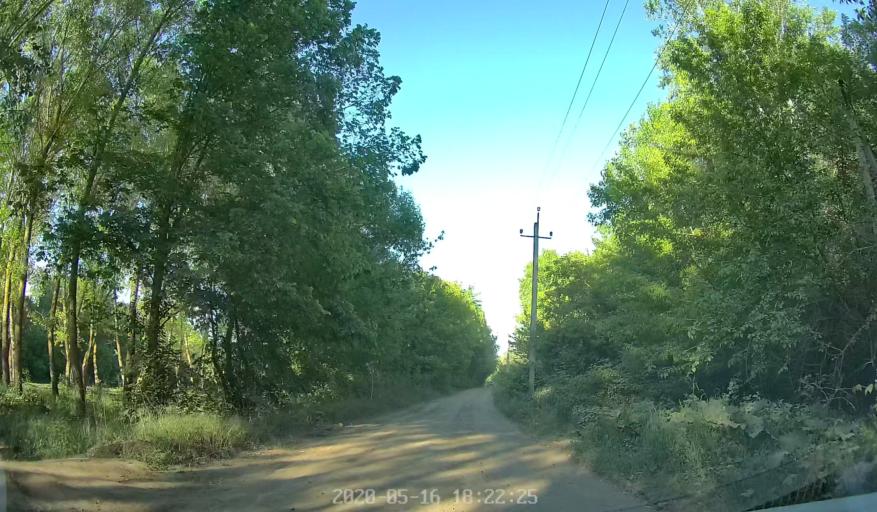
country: MD
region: Telenesti
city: Dnestrovsc
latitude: 46.5412
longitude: 29.9826
